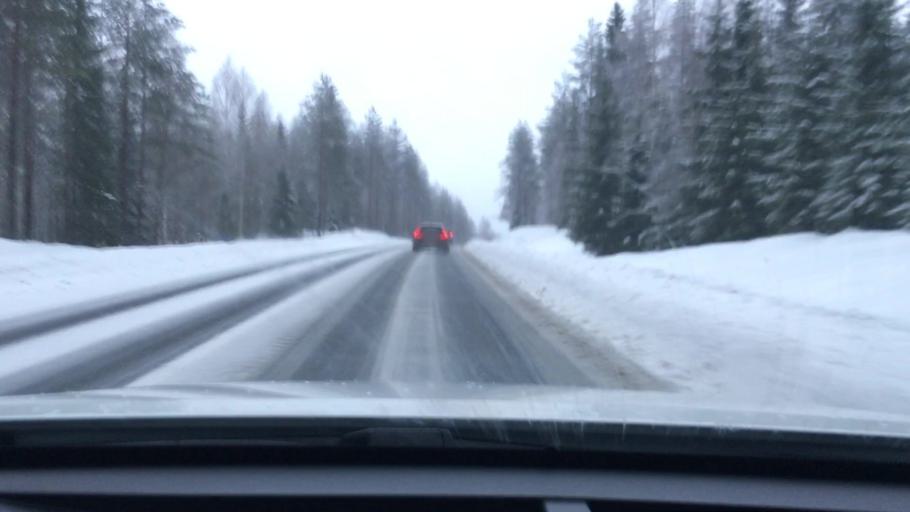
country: FI
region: Northern Savo
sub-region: Ylae-Savo
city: Sonkajaervi
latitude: 63.7669
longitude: 27.4129
